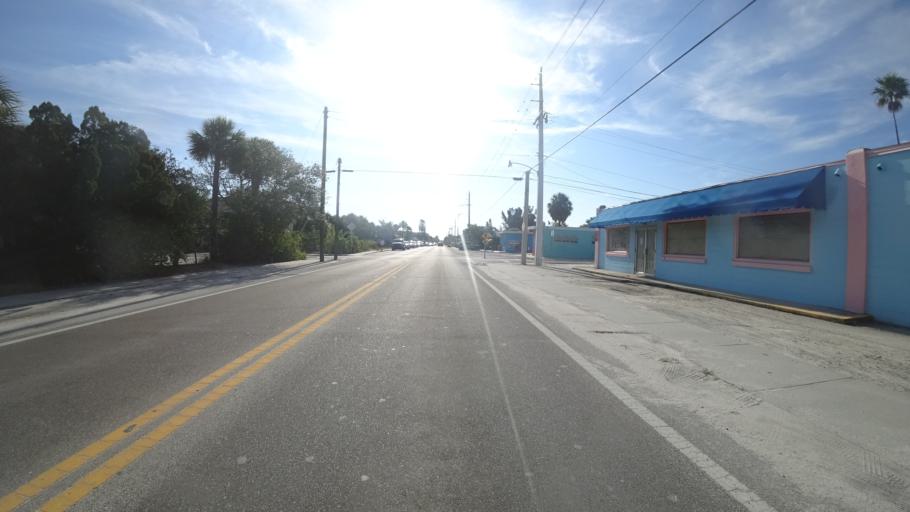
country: US
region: Florida
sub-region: Manatee County
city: Anna Maria
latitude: 27.5265
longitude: -82.7362
